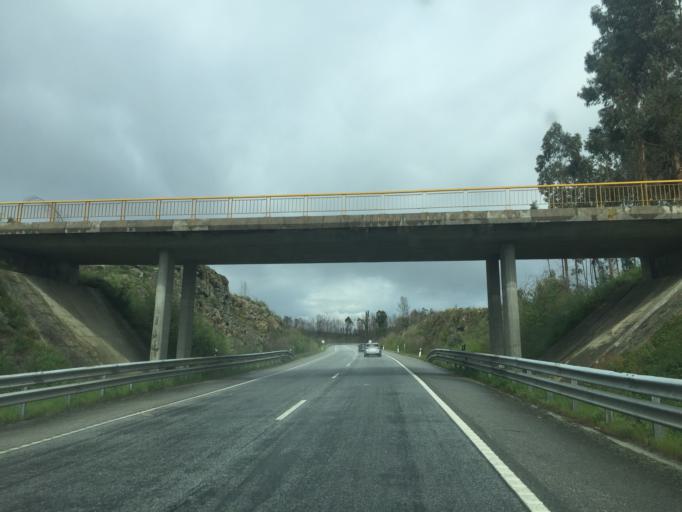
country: PT
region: Viseu
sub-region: Vouzela
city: Vouzela
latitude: 40.6537
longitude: -8.0311
